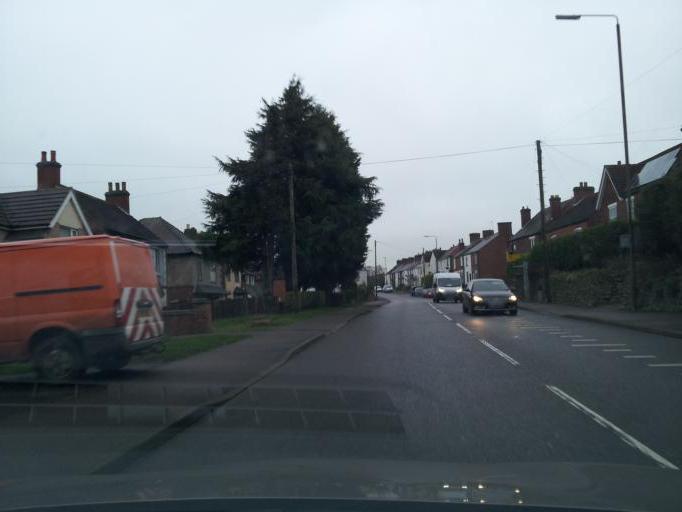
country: GB
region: England
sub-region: Derbyshire
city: Netherseal
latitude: 52.7362
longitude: -1.5657
